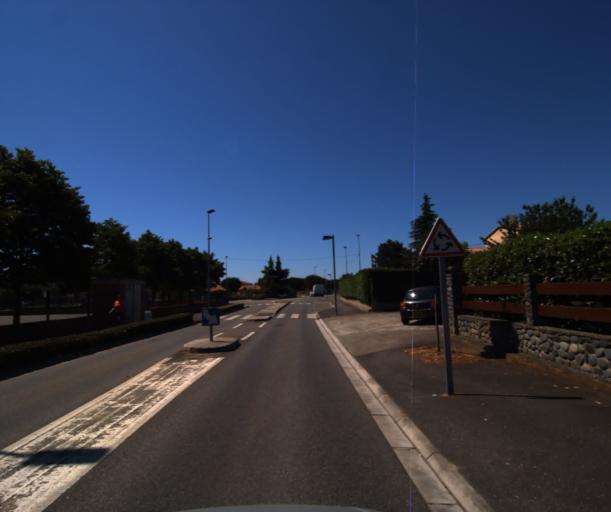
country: FR
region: Midi-Pyrenees
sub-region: Departement de la Haute-Garonne
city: Seysses
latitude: 43.4678
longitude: 1.3185
